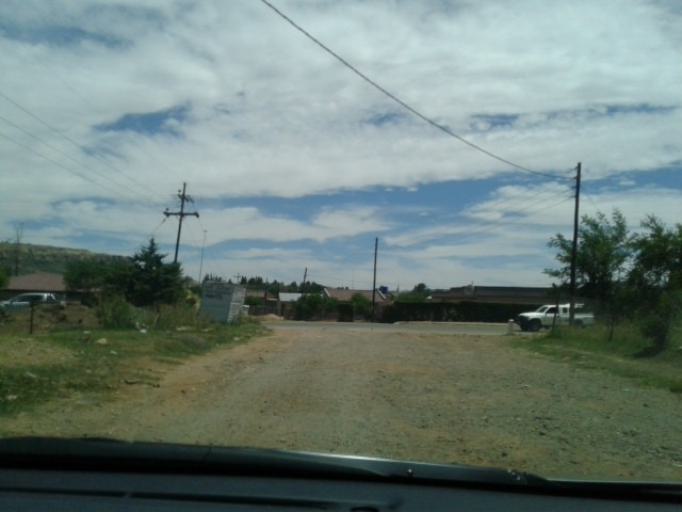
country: LS
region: Maseru
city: Maseru
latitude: -29.2952
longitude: 27.5356
